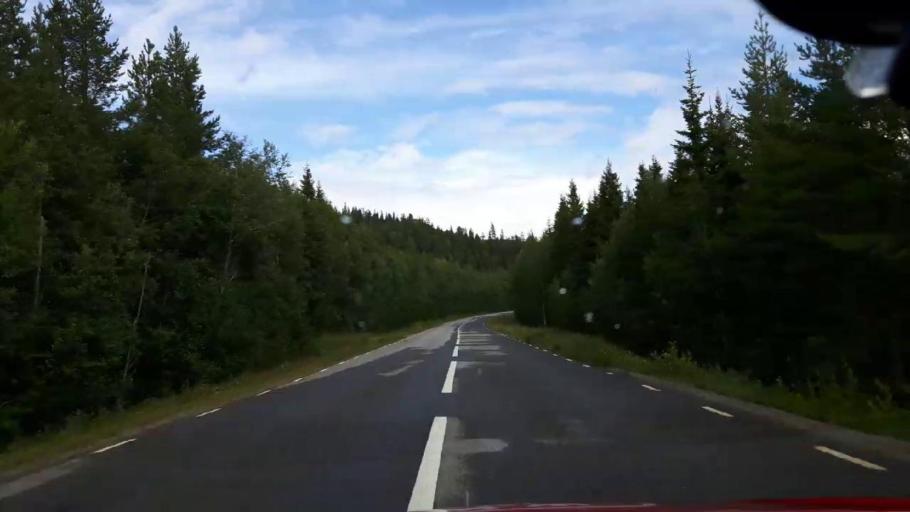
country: SE
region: Jaemtland
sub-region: Stroemsunds Kommun
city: Stroemsund
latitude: 64.3455
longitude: 15.0473
